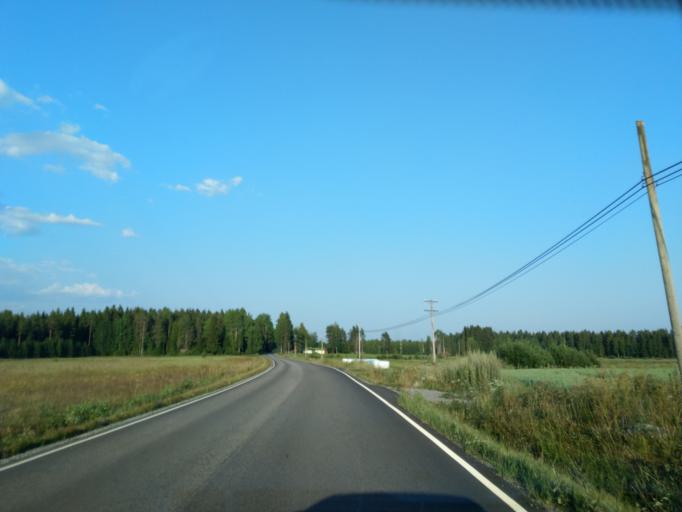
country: FI
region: Satakunta
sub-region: Pohjois-Satakunta
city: Honkajoki
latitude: 61.8204
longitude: 22.2359
